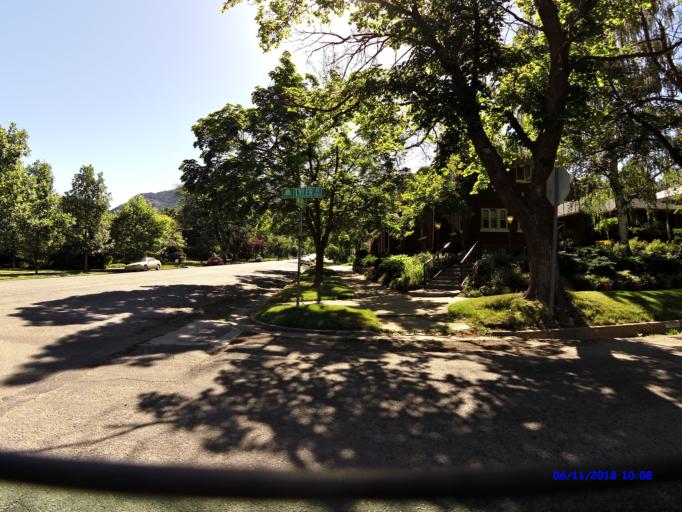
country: US
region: Utah
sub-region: Weber County
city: Ogden
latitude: 41.2202
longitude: -111.9455
